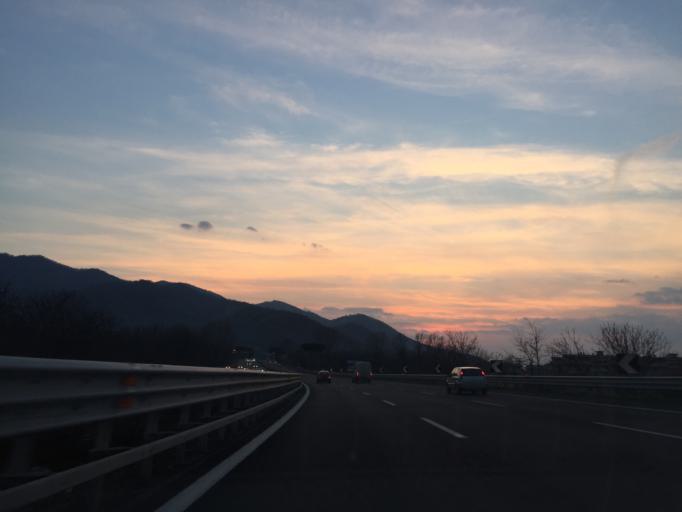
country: IT
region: Campania
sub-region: Provincia di Salerno
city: Faraldo-Nocelleto
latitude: 40.7741
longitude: 14.7586
